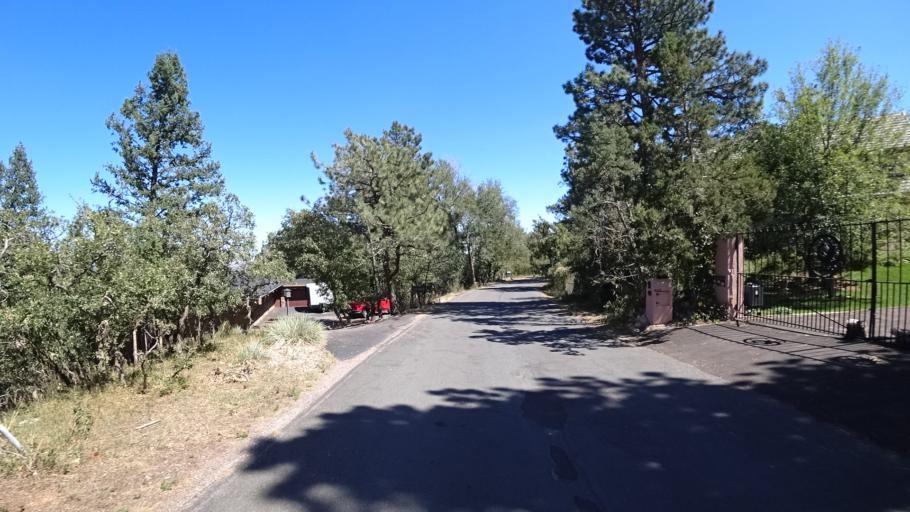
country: US
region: Colorado
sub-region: El Paso County
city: Colorado Springs
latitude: 38.7797
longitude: -104.8578
